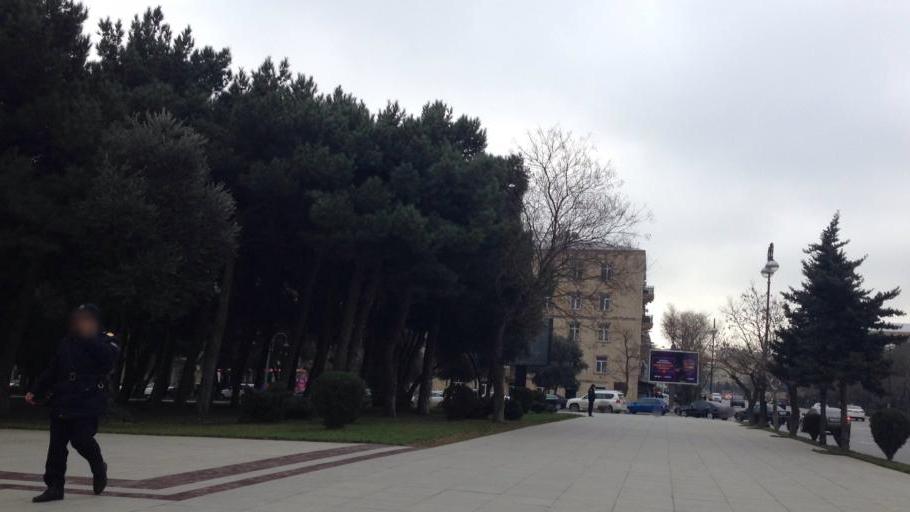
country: AZ
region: Baki
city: Badamdar
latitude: 40.3734
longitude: 49.8163
